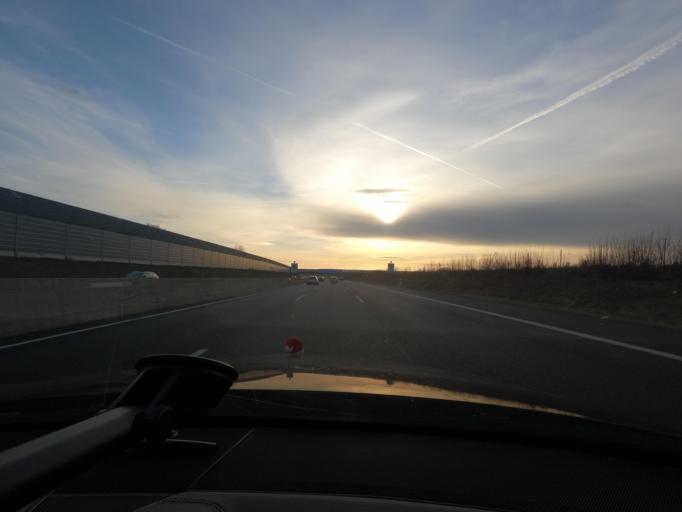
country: DE
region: Lower Saxony
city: Bockenem
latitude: 52.0074
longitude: 10.1596
